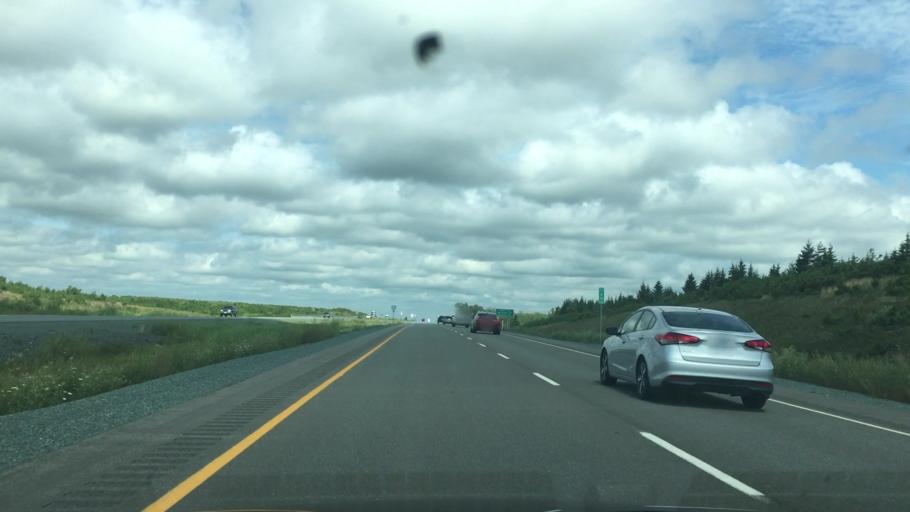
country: CA
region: Nova Scotia
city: Oxford
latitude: 45.6174
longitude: -63.7402
